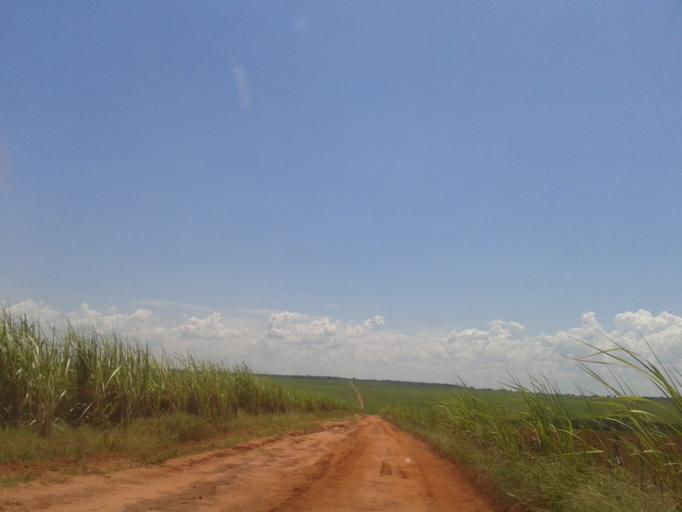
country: BR
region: Minas Gerais
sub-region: Santa Vitoria
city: Santa Vitoria
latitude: -19.1687
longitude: -50.4271
